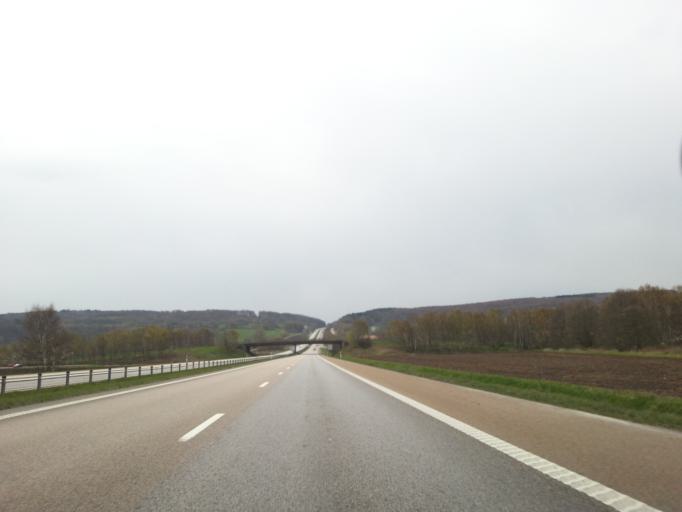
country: SE
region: Halland
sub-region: Laholms Kommun
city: Mellbystrand
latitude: 56.4301
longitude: 12.9520
